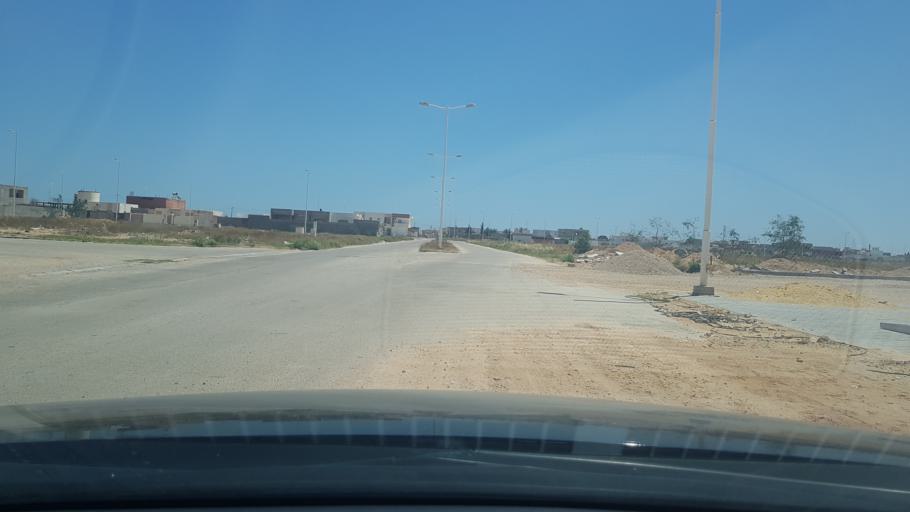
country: TN
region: Safaqis
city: Al Qarmadah
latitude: 34.8321
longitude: 10.7478
